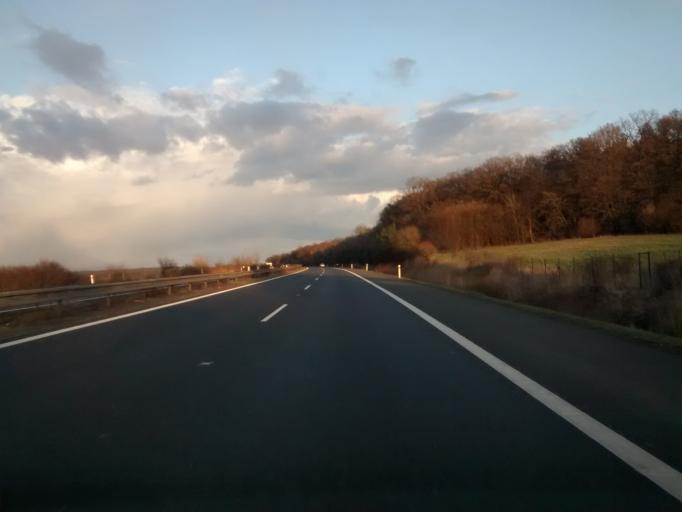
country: CZ
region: Central Bohemia
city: Poricany
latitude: 50.1302
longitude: 14.8705
